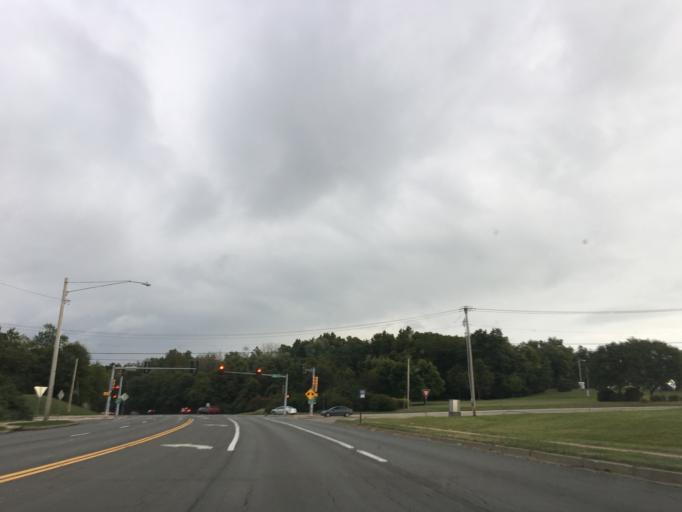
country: US
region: Missouri
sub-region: Saint Louis County
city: Maryland Heights
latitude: 38.7091
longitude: -90.4154
